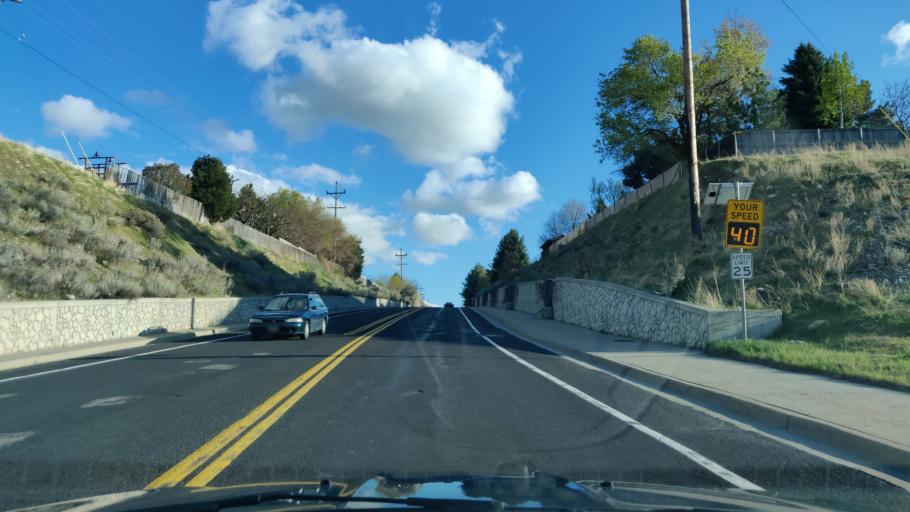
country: US
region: Utah
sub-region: Salt Lake County
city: Cottonwood Heights
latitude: 40.6283
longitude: -111.8077
